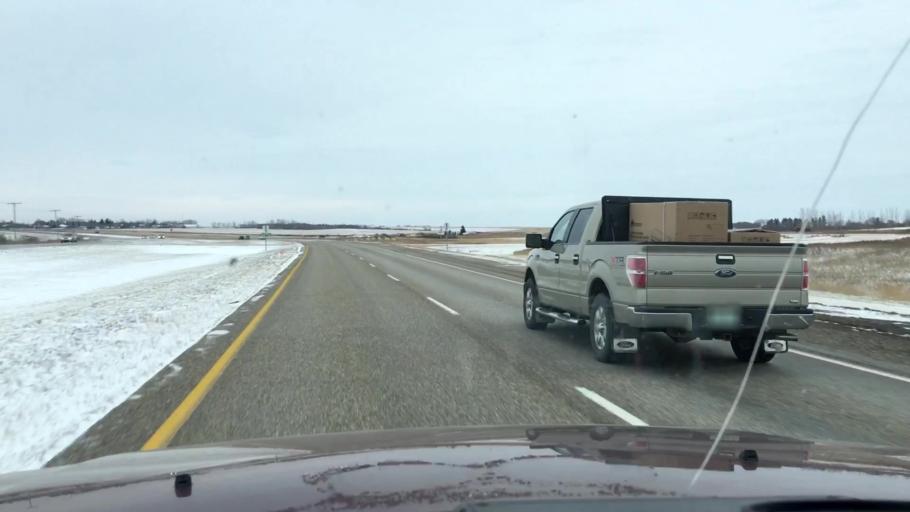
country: CA
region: Saskatchewan
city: Moose Jaw
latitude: 50.9513
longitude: -105.7077
